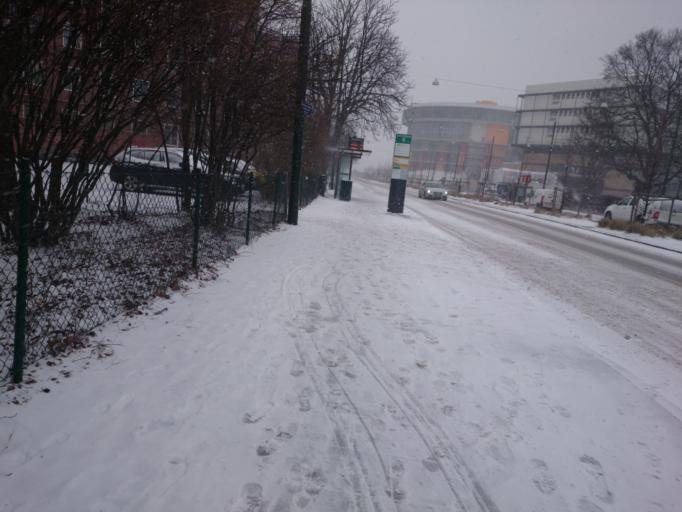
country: SE
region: Skane
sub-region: Malmo
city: Malmoe
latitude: 55.5913
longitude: 13.0005
